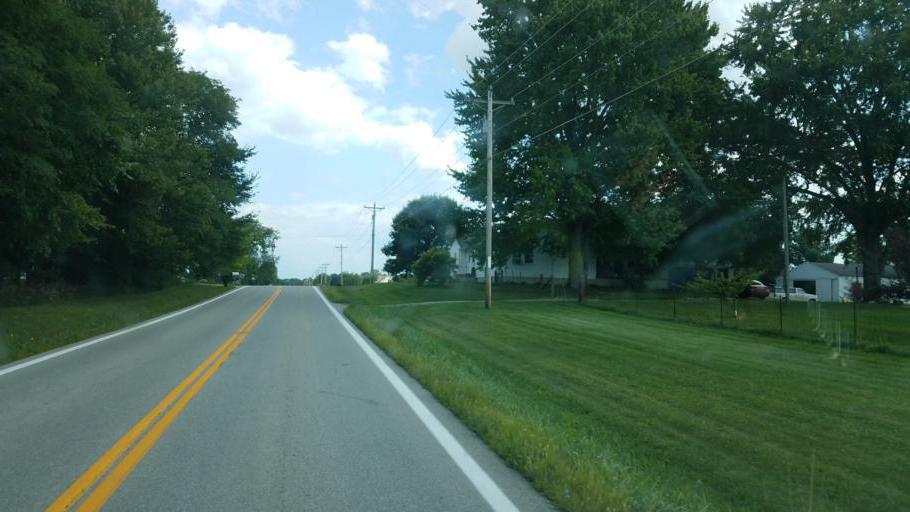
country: US
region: Ohio
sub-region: Delaware County
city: Sunbury
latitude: 40.3250
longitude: -82.8855
